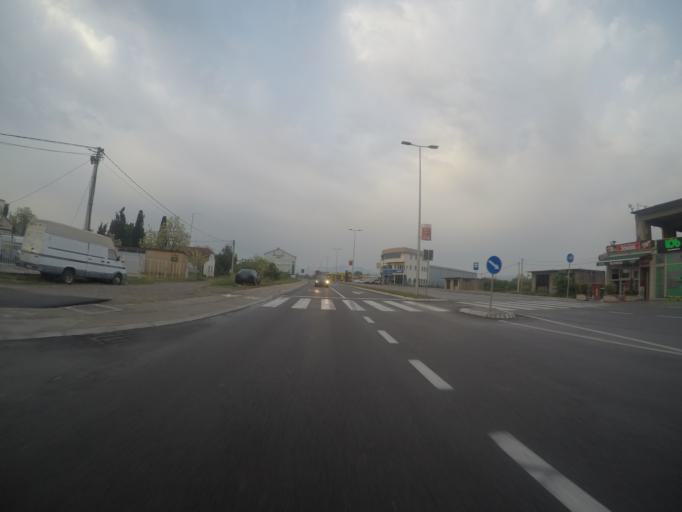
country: ME
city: Mojanovici
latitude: 42.3584
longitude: 19.2238
